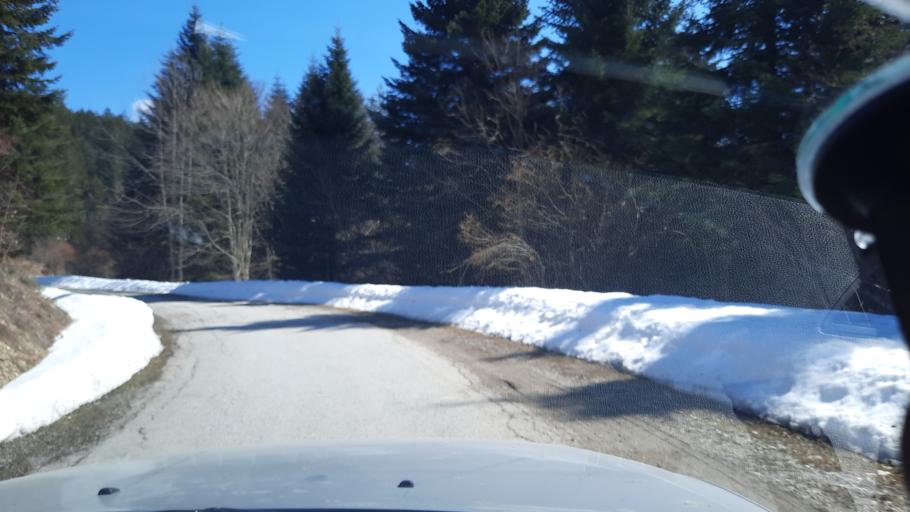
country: MK
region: Gostivar
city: Vrutok
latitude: 41.7042
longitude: 20.7401
